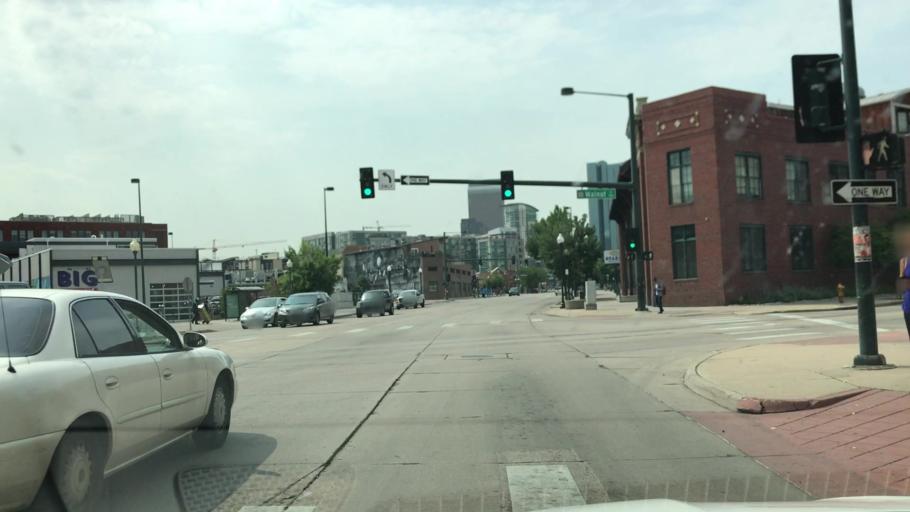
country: US
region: Colorado
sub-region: Denver County
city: Denver
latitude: 39.7584
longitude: -104.9875
